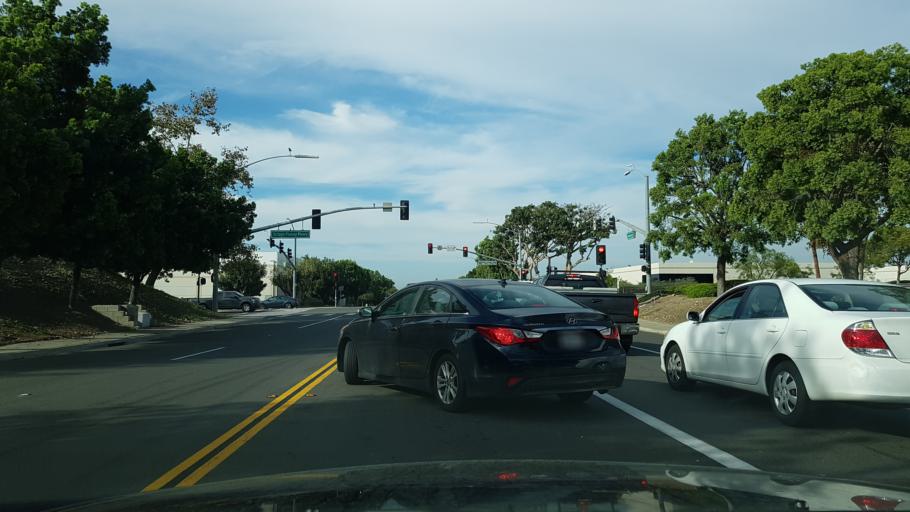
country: US
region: California
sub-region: San Diego County
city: Poway
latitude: 32.9388
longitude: -117.0506
